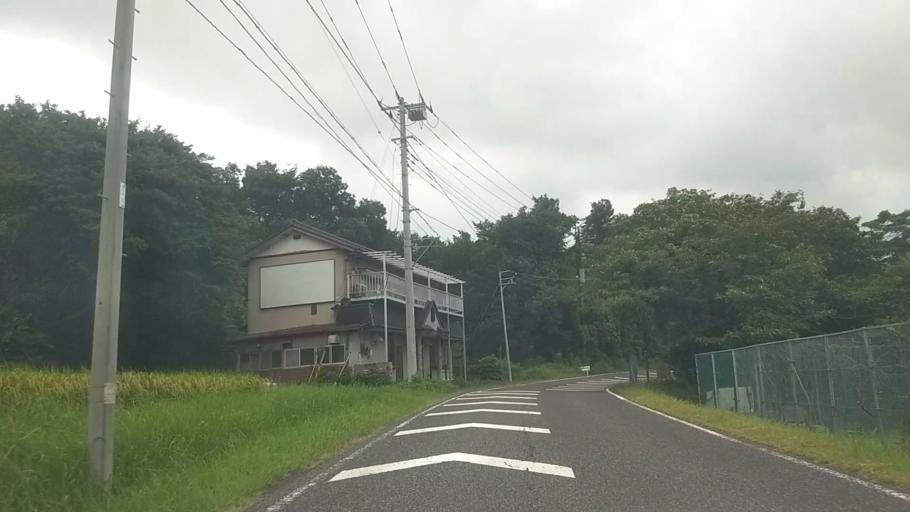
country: JP
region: Chiba
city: Kawaguchi
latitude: 35.2232
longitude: 140.0206
